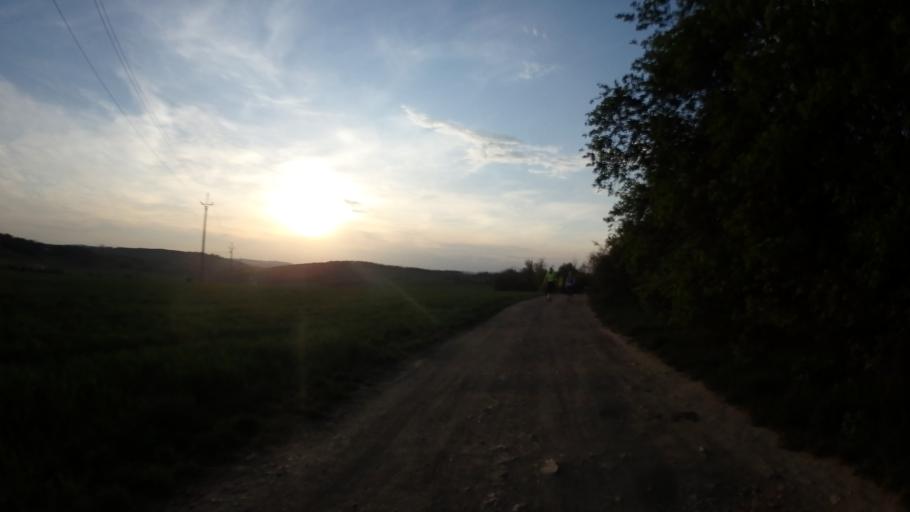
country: CZ
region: South Moravian
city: Ostopovice
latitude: 49.1454
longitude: 16.5548
